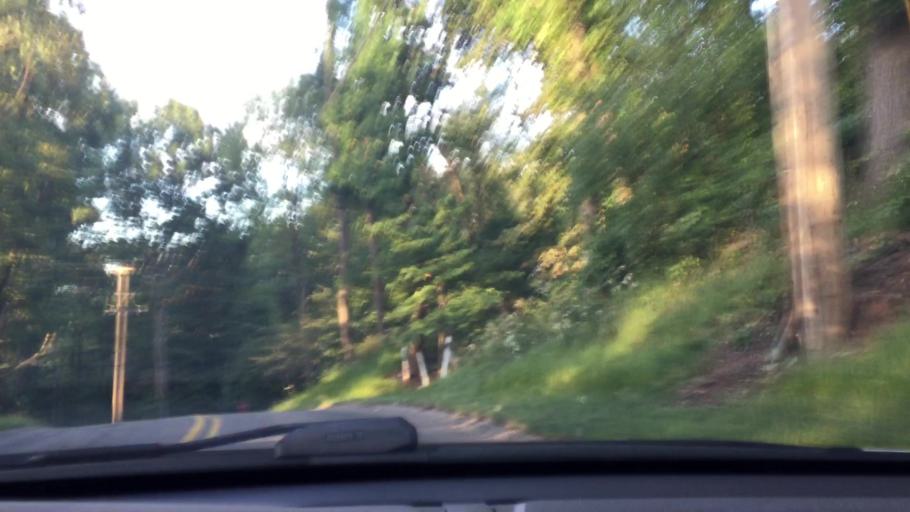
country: US
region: Pennsylvania
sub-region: Allegheny County
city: Plum
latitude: 40.4560
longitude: -79.7448
